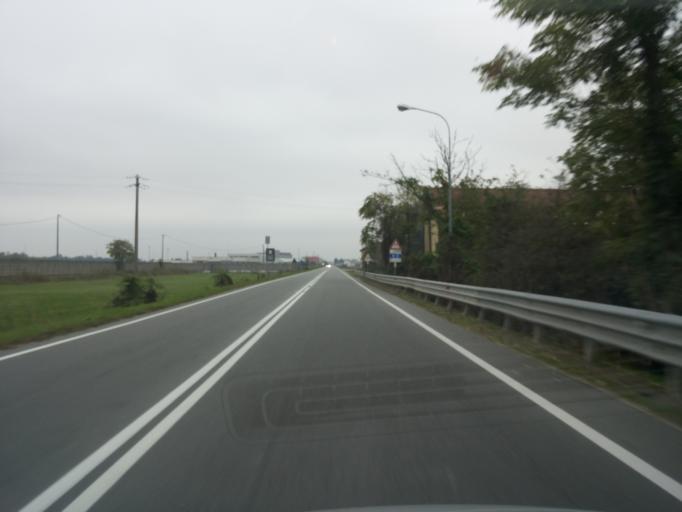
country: IT
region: Piedmont
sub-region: Provincia di Vercelli
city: Vercelli
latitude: 45.3274
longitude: 8.4471
